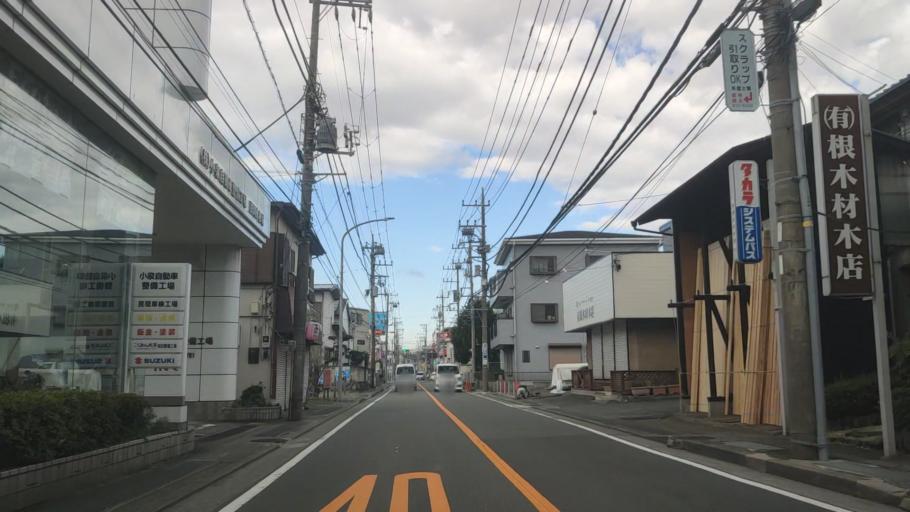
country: JP
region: Kanagawa
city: Fujisawa
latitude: 35.4225
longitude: 139.5328
